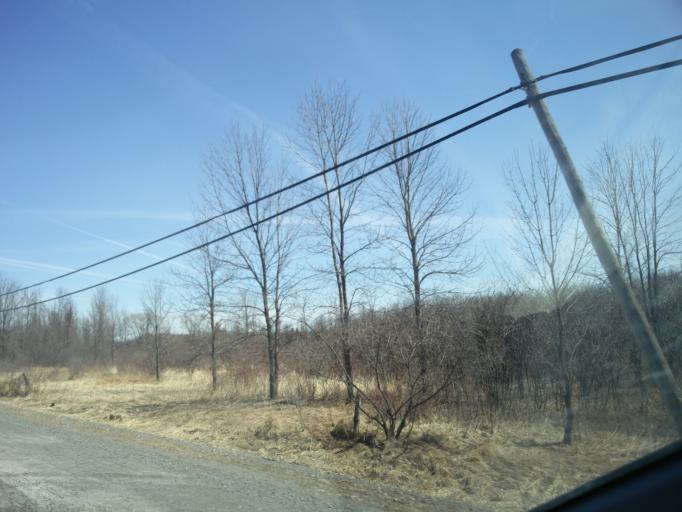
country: CA
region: Ontario
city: Bells Corners
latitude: 45.1784
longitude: -75.6390
